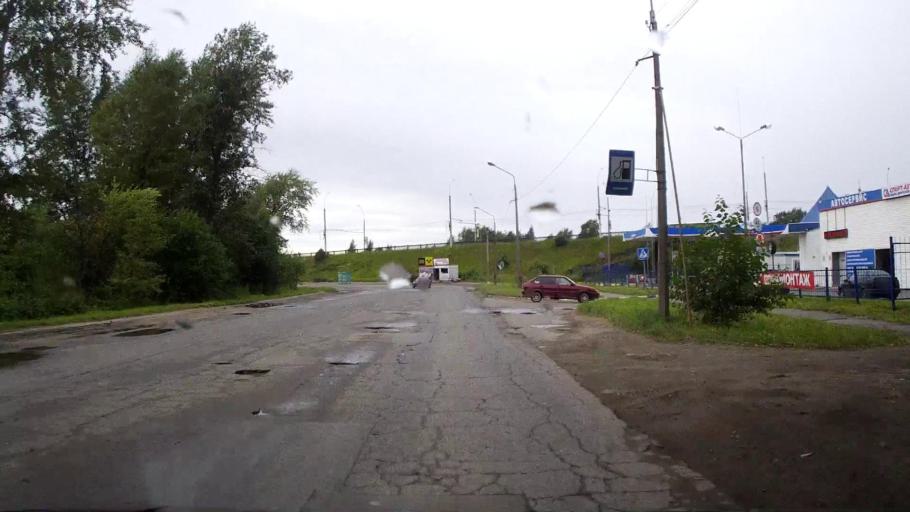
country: RU
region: Vologda
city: Vologda
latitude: 59.2056
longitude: 39.8784
